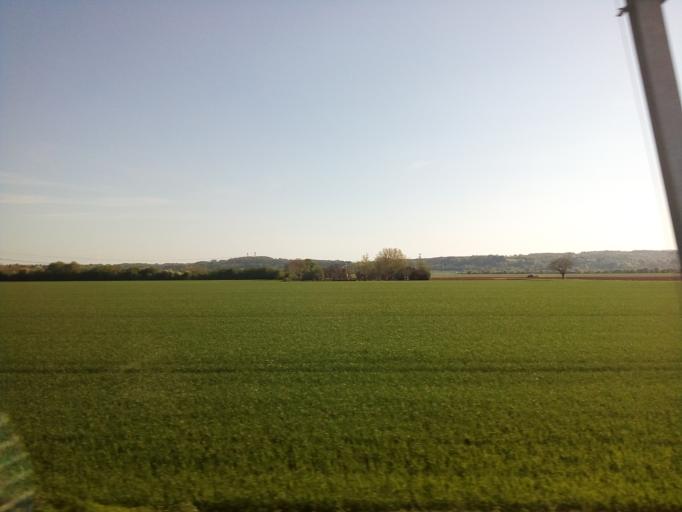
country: FR
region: Rhone-Alpes
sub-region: Departement du Rhone
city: Saint-Laurent-de-Mure
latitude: 45.6597
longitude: 5.0462
